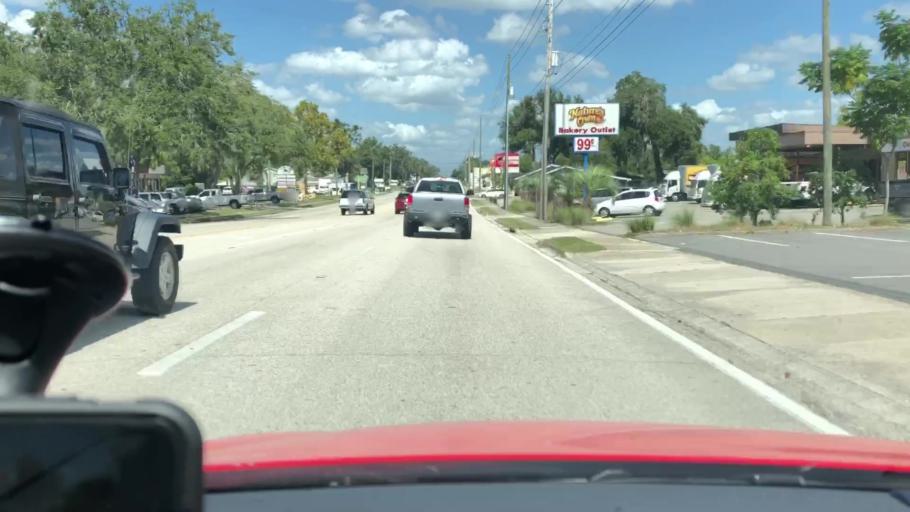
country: US
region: Florida
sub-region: Volusia County
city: West DeLand
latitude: 29.0231
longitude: -81.3240
